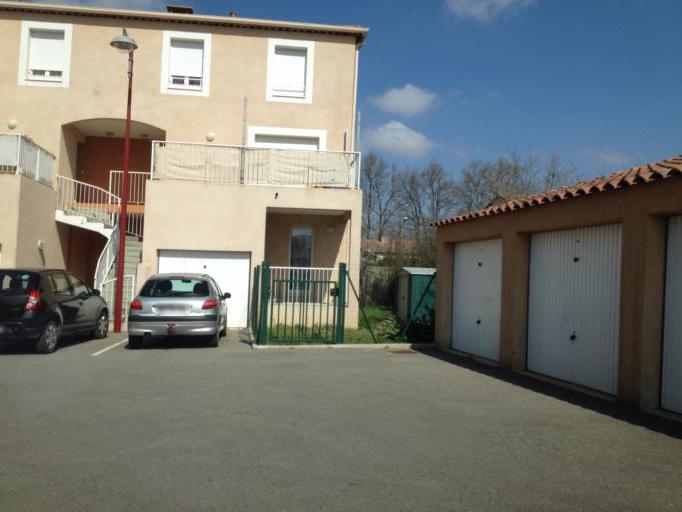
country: FR
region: Provence-Alpes-Cote d'Azur
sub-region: Departement du Vaucluse
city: Jonquieres
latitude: 44.1183
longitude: 4.9025
